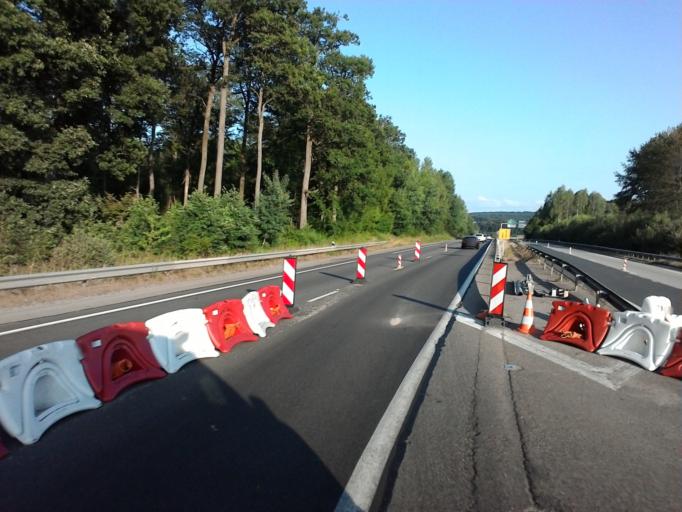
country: FR
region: Lorraine
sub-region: Departement des Vosges
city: Dogneville
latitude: 48.2025
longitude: 6.4672
